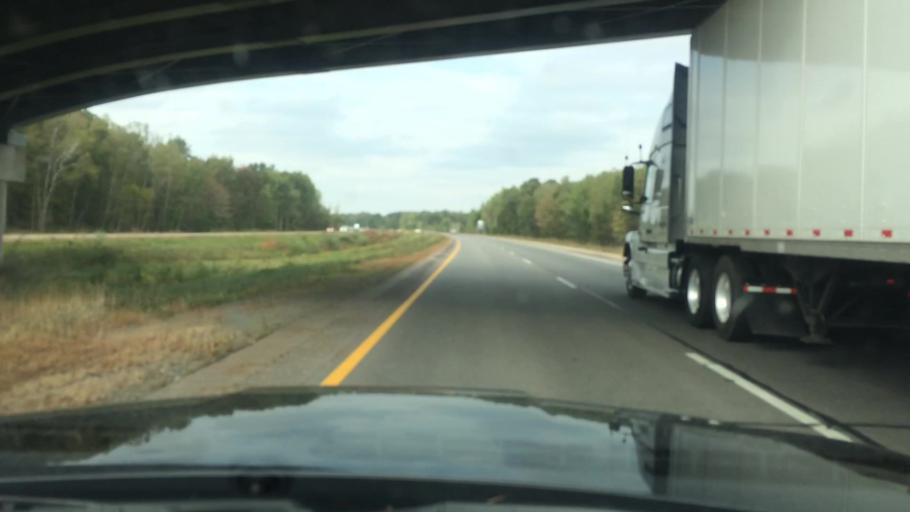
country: US
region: Wisconsin
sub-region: Marathon County
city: Mosinee
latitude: 44.7138
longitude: -89.6599
